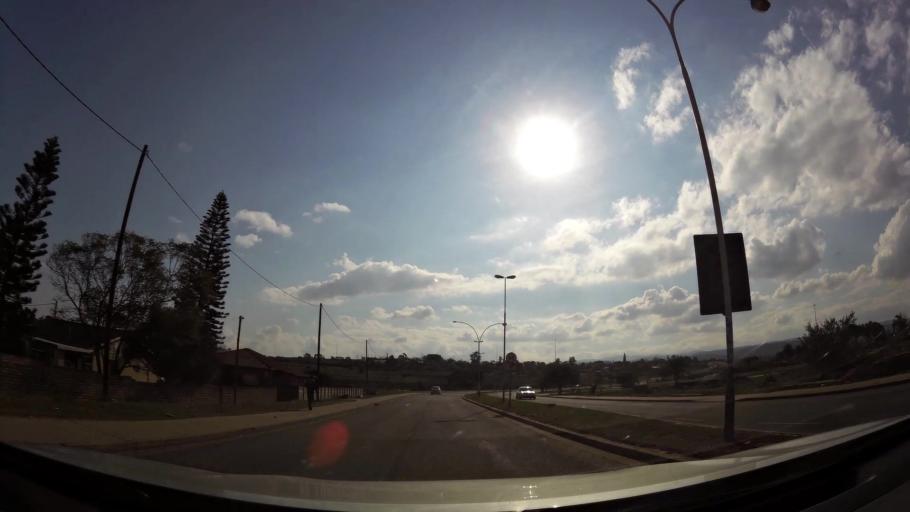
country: ZA
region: Eastern Cape
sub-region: Nelson Mandela Bay Metropolitan Municipality
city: Uitenhage
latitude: -33.7600
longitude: 25.3895
